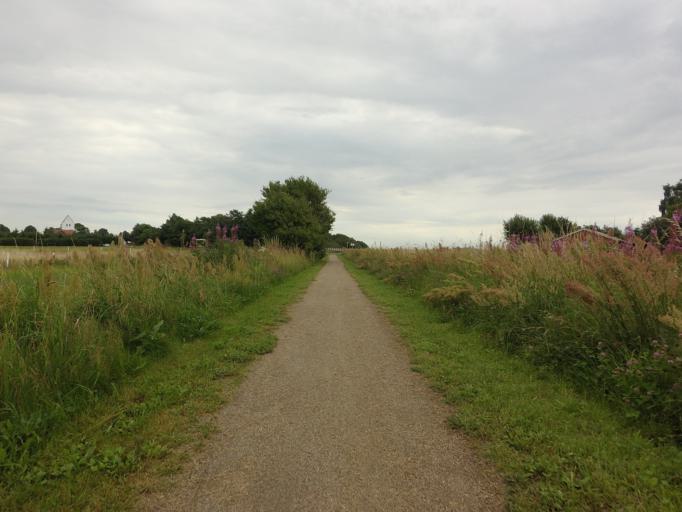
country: DK
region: North Denmark
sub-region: Alborg Kommune
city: Vadum
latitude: 57.1133
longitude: 9.8801
